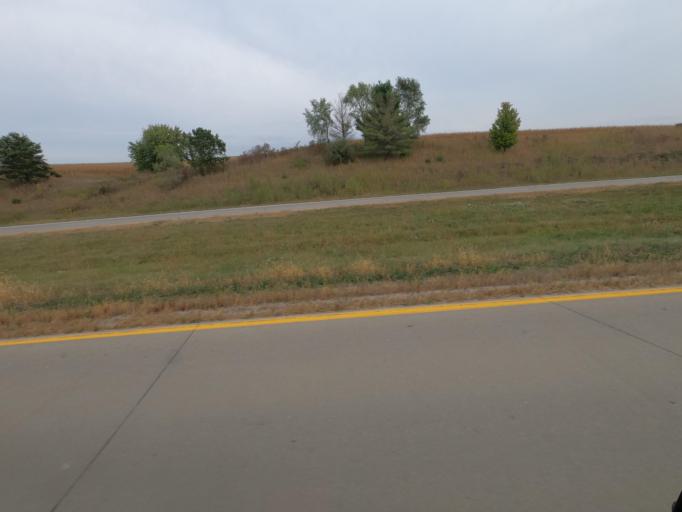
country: US
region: Iowa
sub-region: Marion County
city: Pella
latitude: 41.3932
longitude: -92.9287
